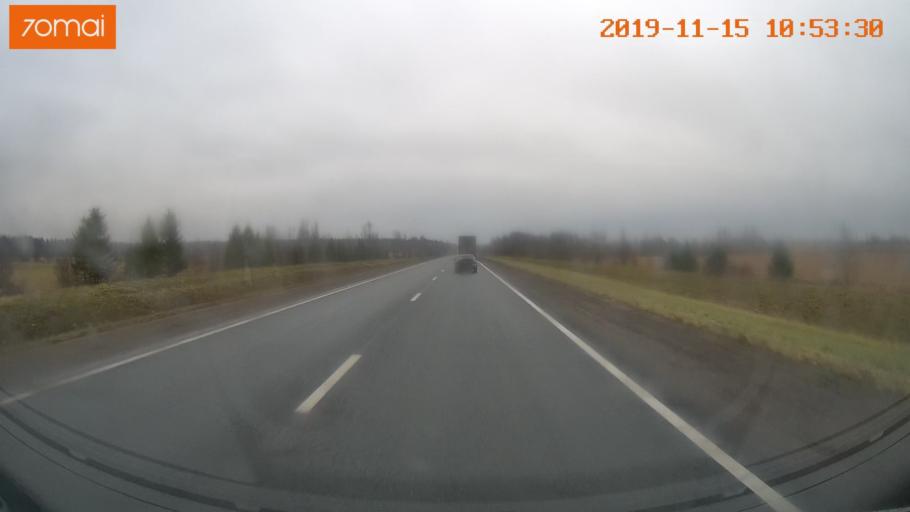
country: RU
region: Vologda
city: Chebsara
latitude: 59.1689
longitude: 38.7558
